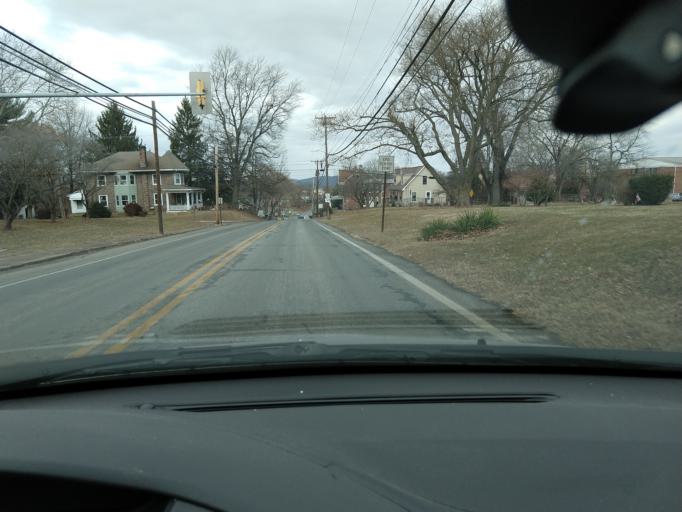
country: US
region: Pennsylvania
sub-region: Chester County
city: South Pottstown
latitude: 40.2309
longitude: -75.6547
